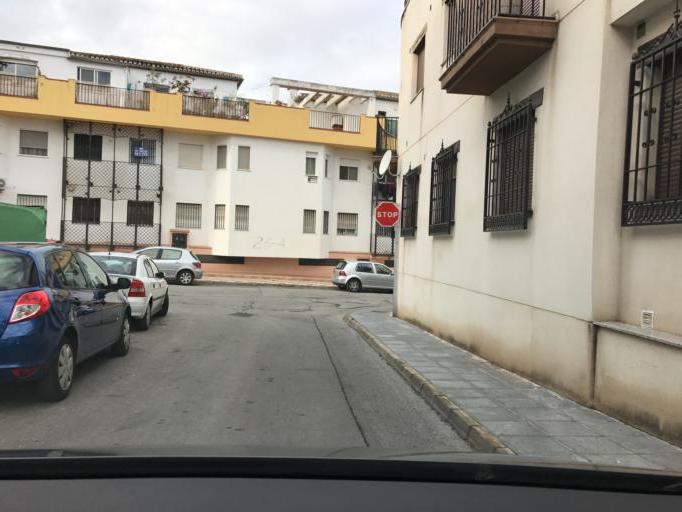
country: ES
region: Andalusia
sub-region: Provincia de Granada
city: Zubia
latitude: 37.1214
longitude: -3.5908
